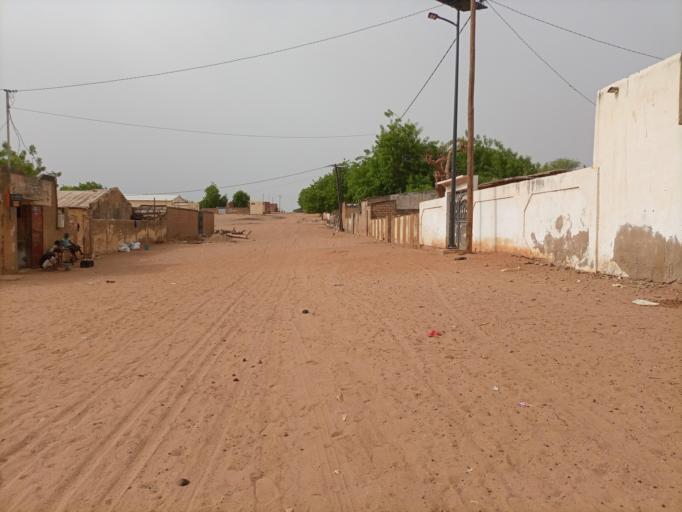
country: SN
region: Louga
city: Ndibene Dahra
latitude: 15.4011
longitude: -15.1175
